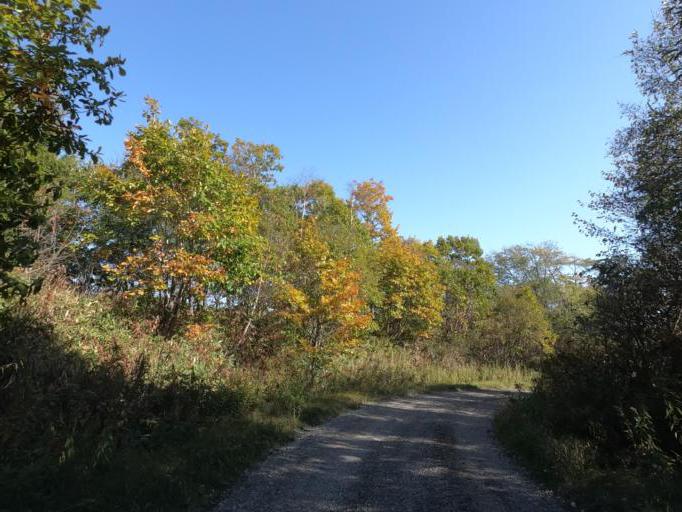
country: JP
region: Hokkaido
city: Obihiro
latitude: 42.7276
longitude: 143.4537
